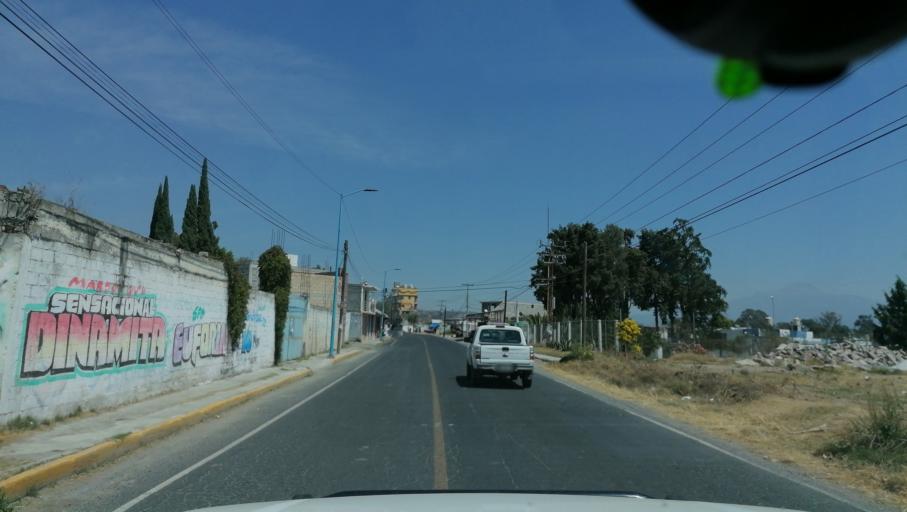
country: MX
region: Tlaxcala
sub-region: Tetlatlahuca
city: Tetlatlahuca
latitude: 19.2325
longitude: -98.2878
